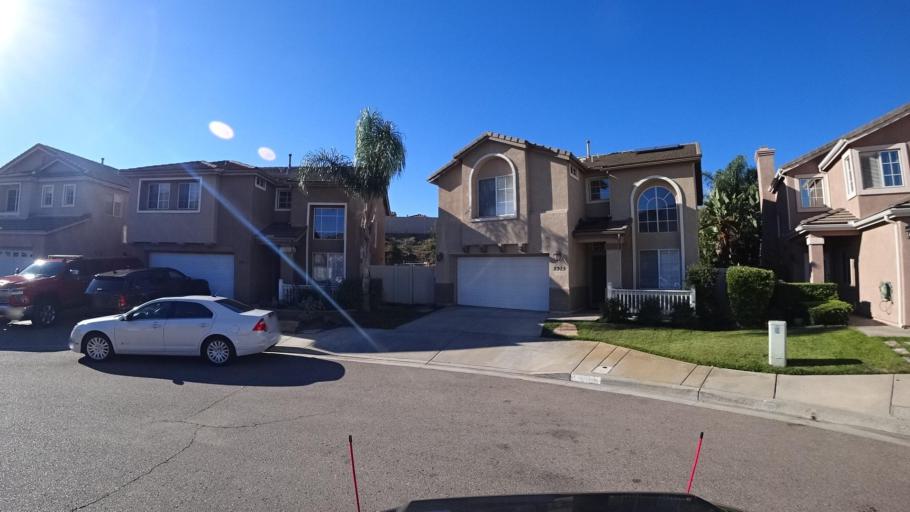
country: US
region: California
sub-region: San Diego County
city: Alpine
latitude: 32.8324
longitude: -116.7525
